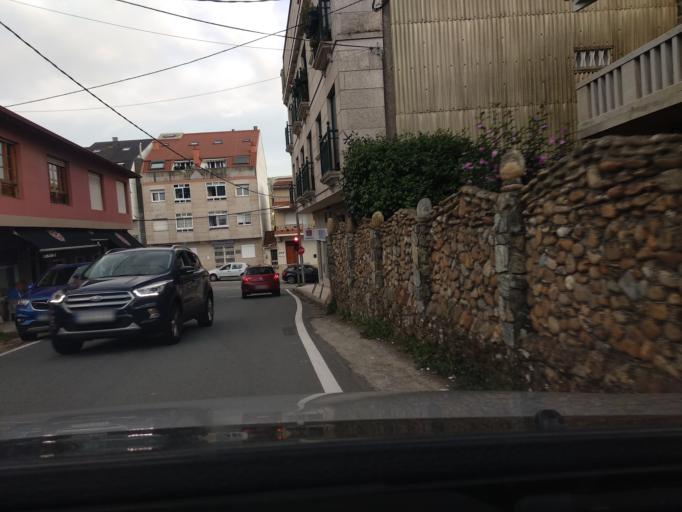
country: ES
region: Galicia
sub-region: Provincia de Pontevedra
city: Vigo
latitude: 42.2862
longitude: -8.6836
